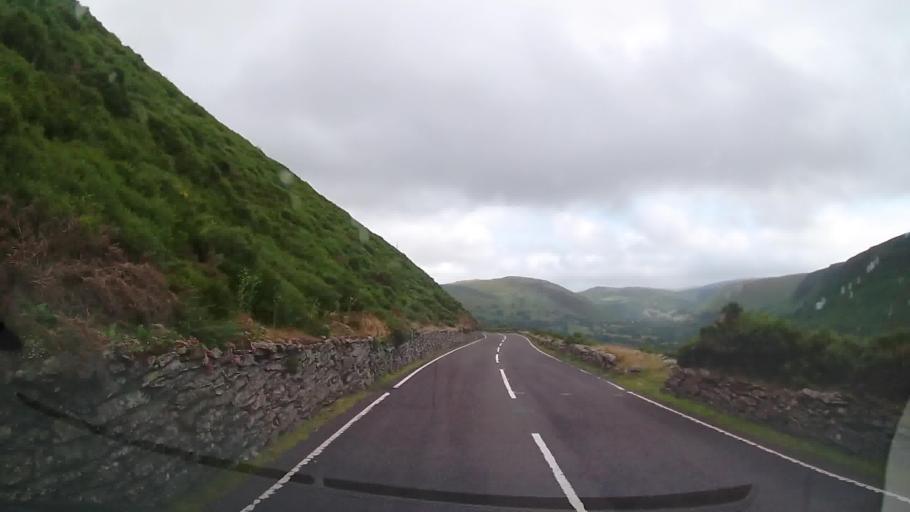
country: GB
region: Wales
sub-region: Sir Powys
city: Llangynog
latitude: 52.8538
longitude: -3.4427
